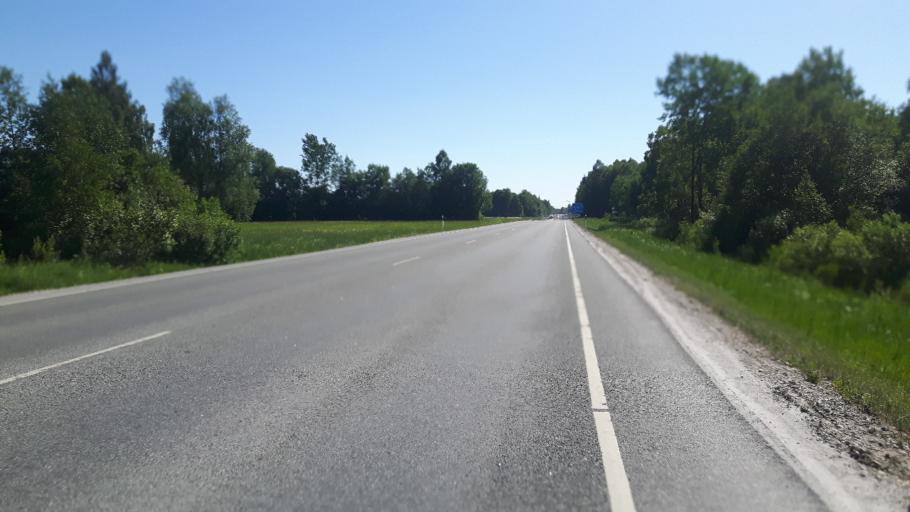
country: EE
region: Raplamaa
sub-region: Rapla vald
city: Rapla
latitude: 59.0195
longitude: 24.8074
